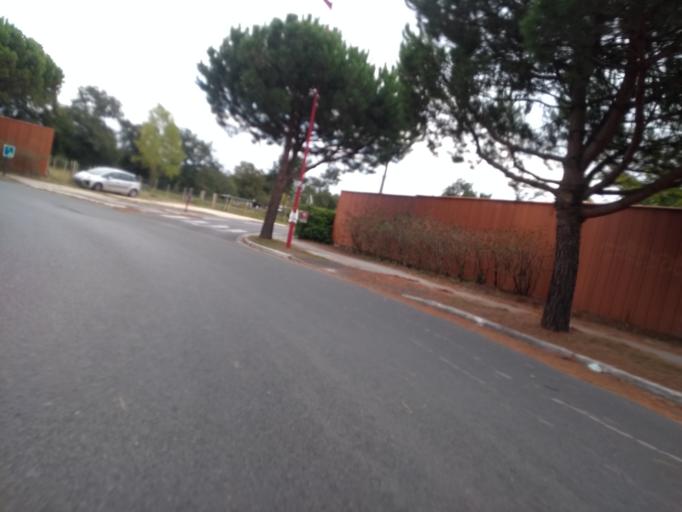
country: FR
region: Aquitaine
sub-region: Departement de la Gironde
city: Pessac
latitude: 44.8190
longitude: -0.6590
